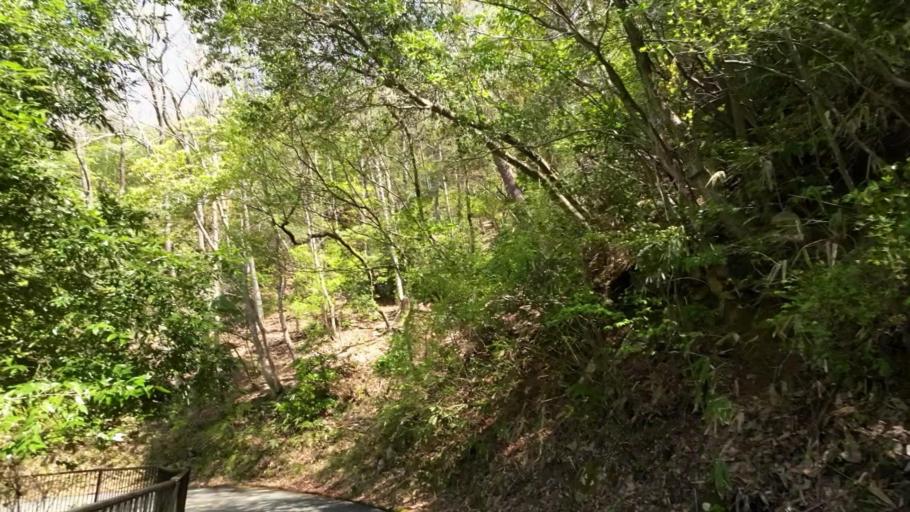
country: JP
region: Hyogo
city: Toyooka
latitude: 35.2988
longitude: 134.8276
